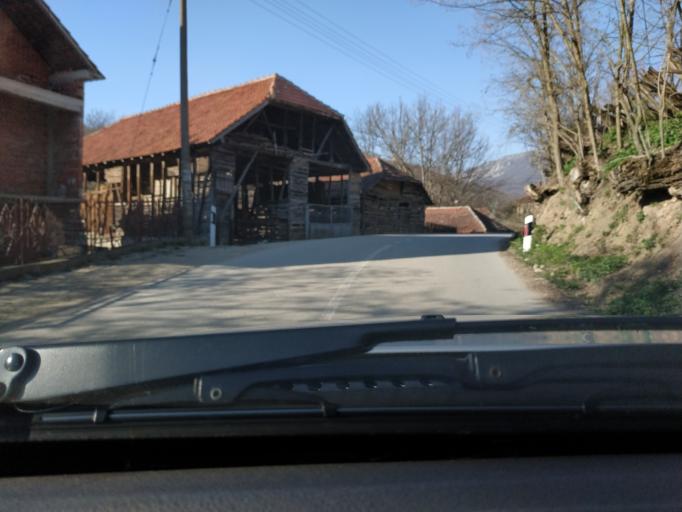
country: RS
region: Central Serbia
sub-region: Nisavski Okrug
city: Aleksinac
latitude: 43.5476
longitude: 21.8107
